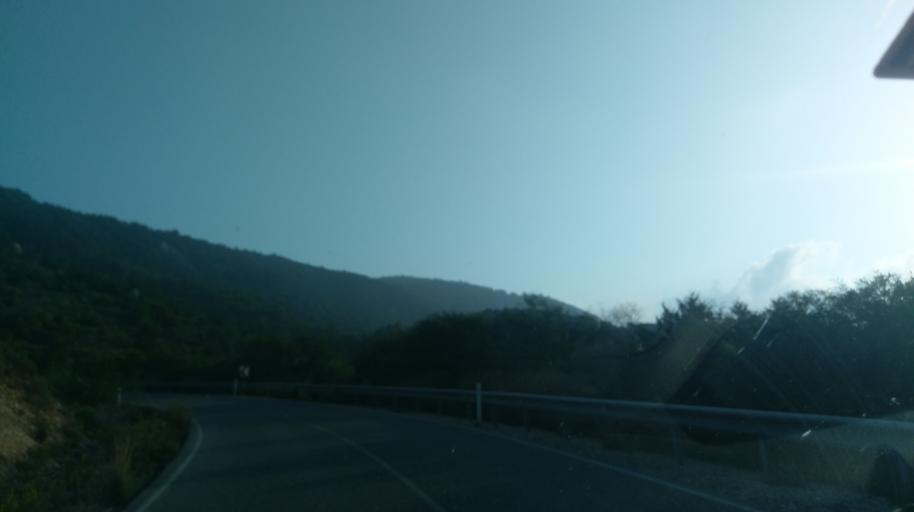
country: CY
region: Ammochostos
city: Trikomo
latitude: 35.4073
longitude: 33.9039
